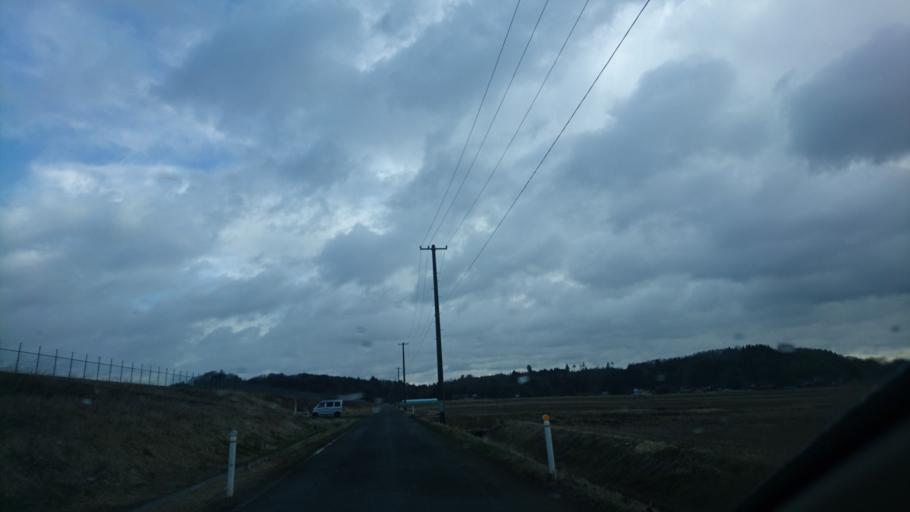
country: JP
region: Iwate
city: Ichinoseki
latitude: 38.7796
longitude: 141.0318
